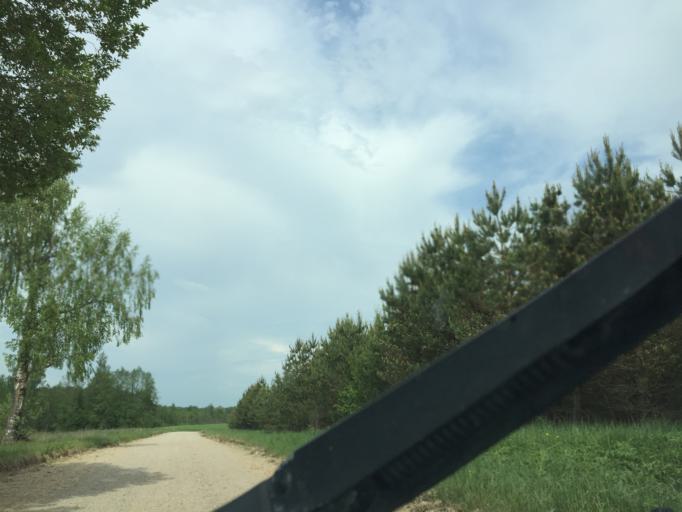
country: LV
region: Livani
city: Livani
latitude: 56.5766
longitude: 26.1732
